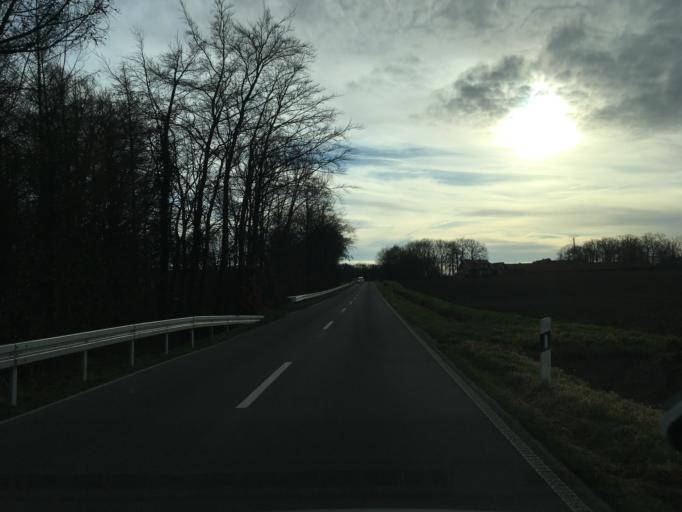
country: DE
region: North Rhine-Westphalia
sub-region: Regierungsbezirk Munster
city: Heek
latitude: 52.0831
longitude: 7.1296
